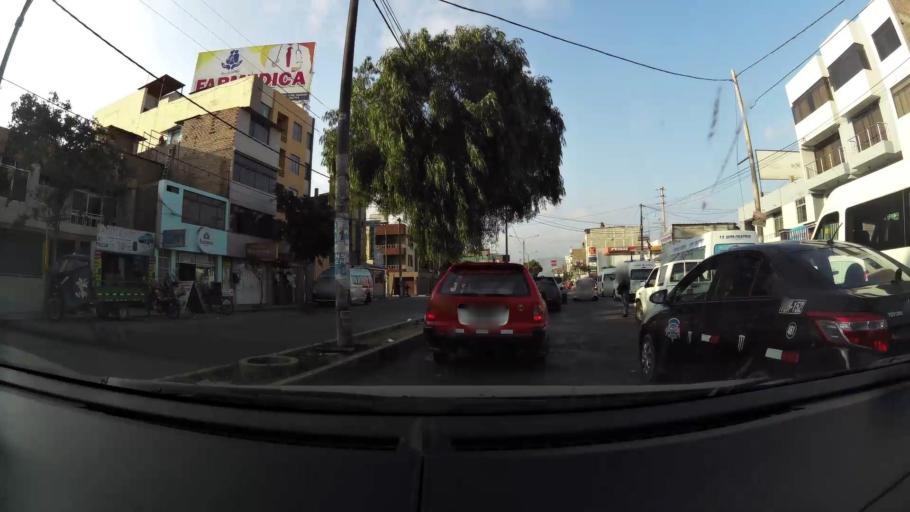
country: PE
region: La Libertad
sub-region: Provincia de Trujillo
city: El Porvenir
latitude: -8.0945
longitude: -79.0094
